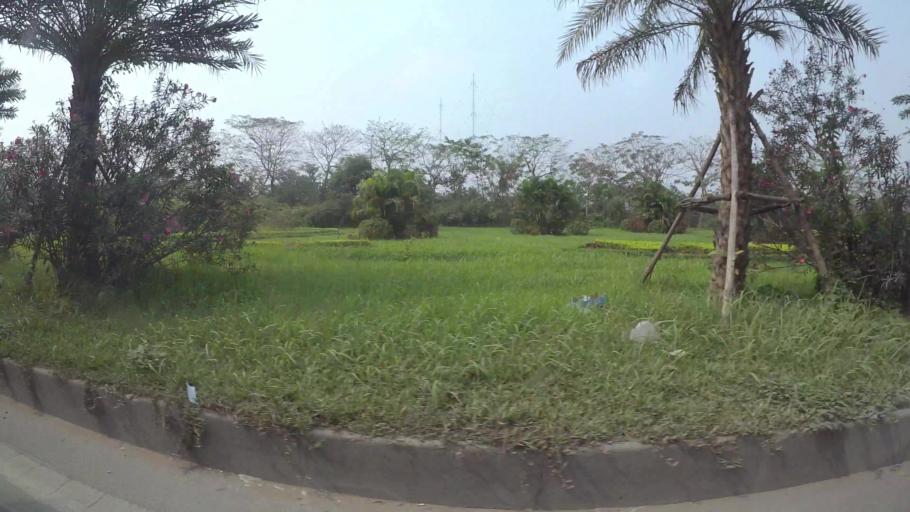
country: VN
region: Ha Noi
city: Thanh Xuan
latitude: 21.0039
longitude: 105.7784
